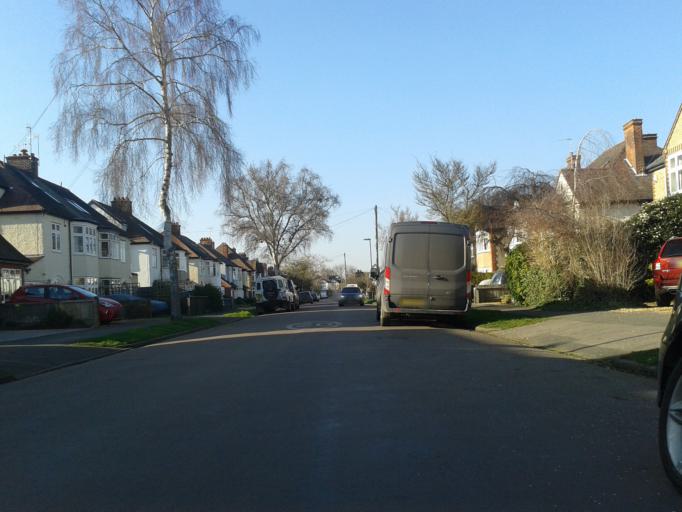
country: GB
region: England
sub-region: Cambridgeshire
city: Cambridge
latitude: 52.2205
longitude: 0.1279
